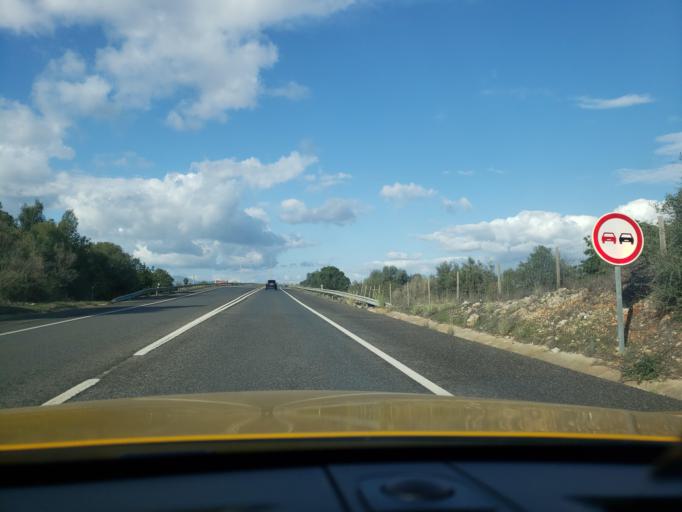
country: PT
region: Faro
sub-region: Silves
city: Silves
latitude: 37.1741
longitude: -8.4435
